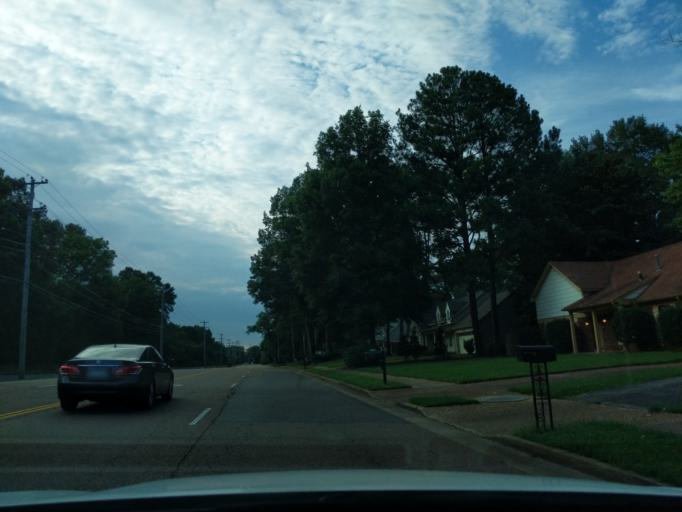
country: US
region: Tennessee
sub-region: Shelby County
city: Germantown
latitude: 35.0772
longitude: -89.7978
